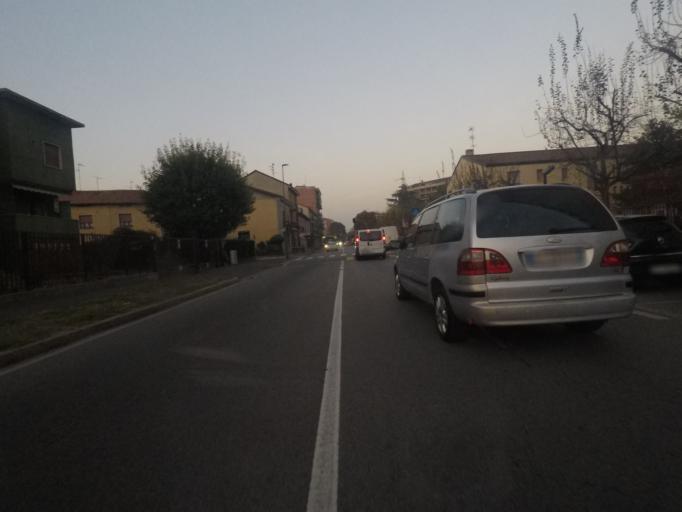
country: IT
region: Lombardy
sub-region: Citta metropolitana di Milano
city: Cologno Monzese
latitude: 45.5221
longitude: 9.2718
